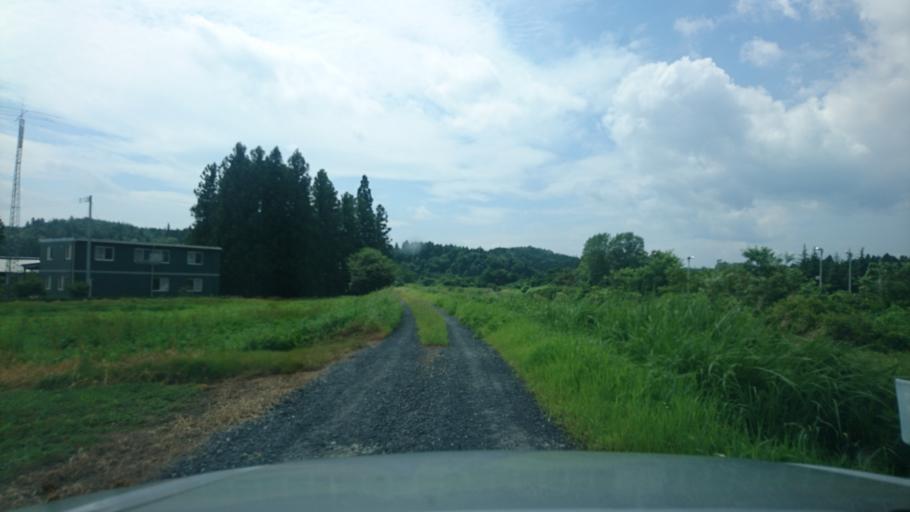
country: JP
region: Iwate
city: Ichinoseki
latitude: 38.8067
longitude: 140.9507
